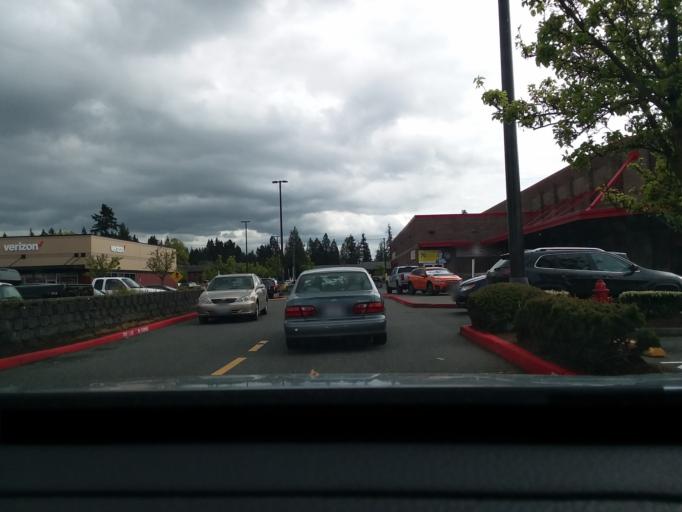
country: US
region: Washington
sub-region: Snohomish County
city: Esperance
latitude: 47.7759
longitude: -122.3440
